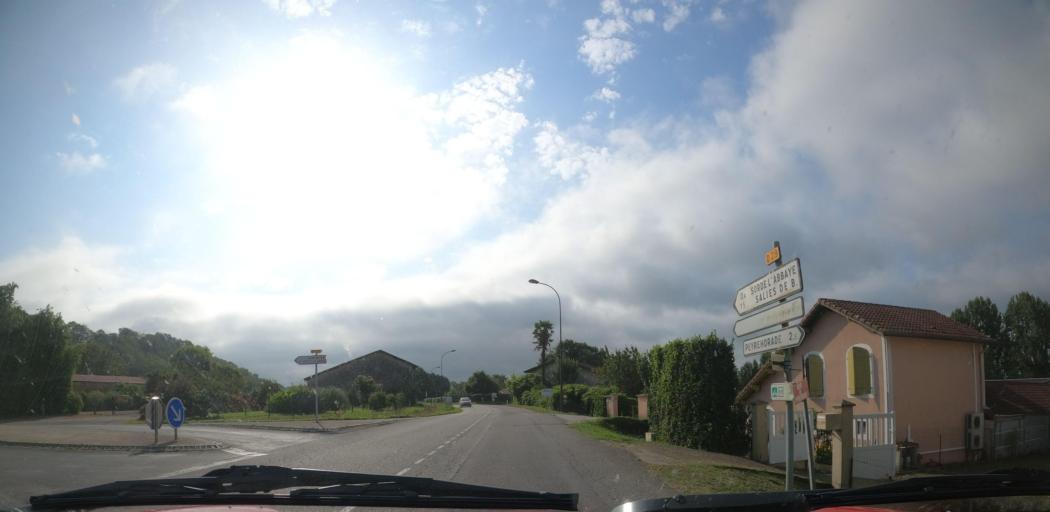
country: FR
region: Aquitaine
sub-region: Departement des Landes
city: Peyrehorade
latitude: 43.5332
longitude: -1.0675
